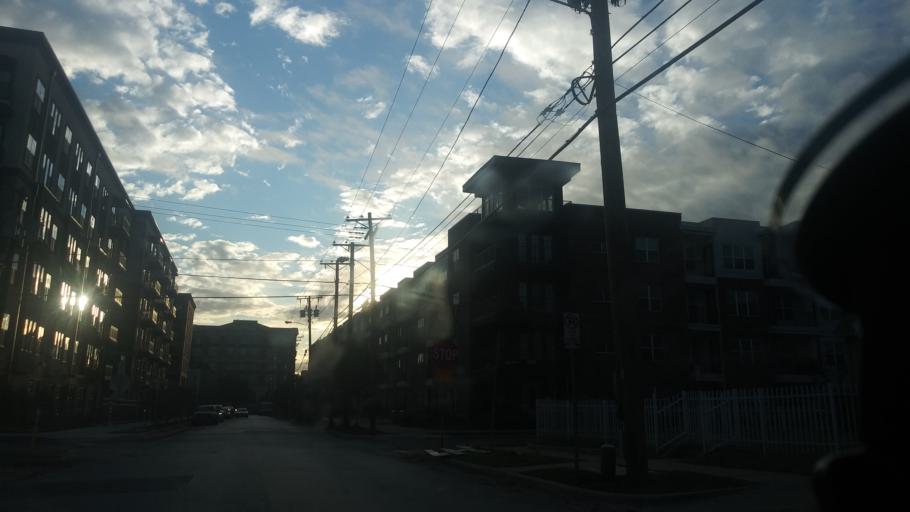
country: US
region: Texas
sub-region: Dallas County
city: Dallas
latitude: 32.8084
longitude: -96.8145
